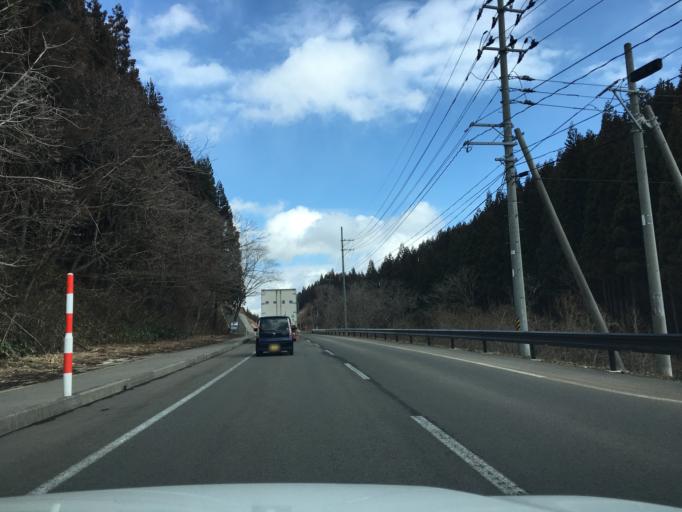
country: JP
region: Akita
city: Takanosu
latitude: 40.1008
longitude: 140.3454
